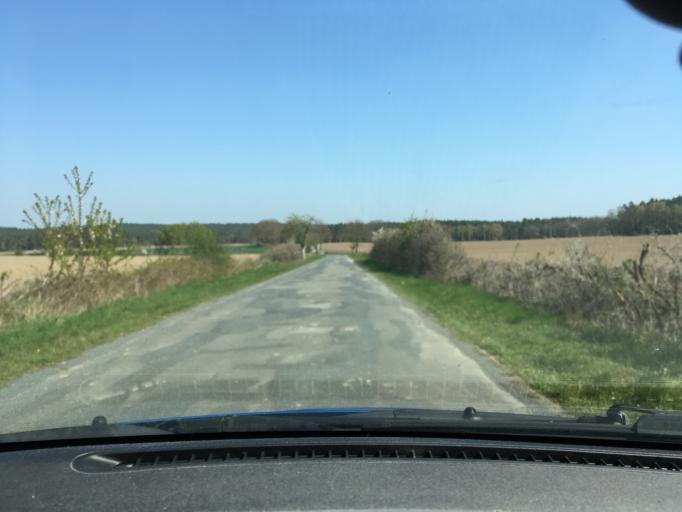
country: DE
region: Lower Saxony
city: Reinstorf
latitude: 53.2001
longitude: 10.5943
